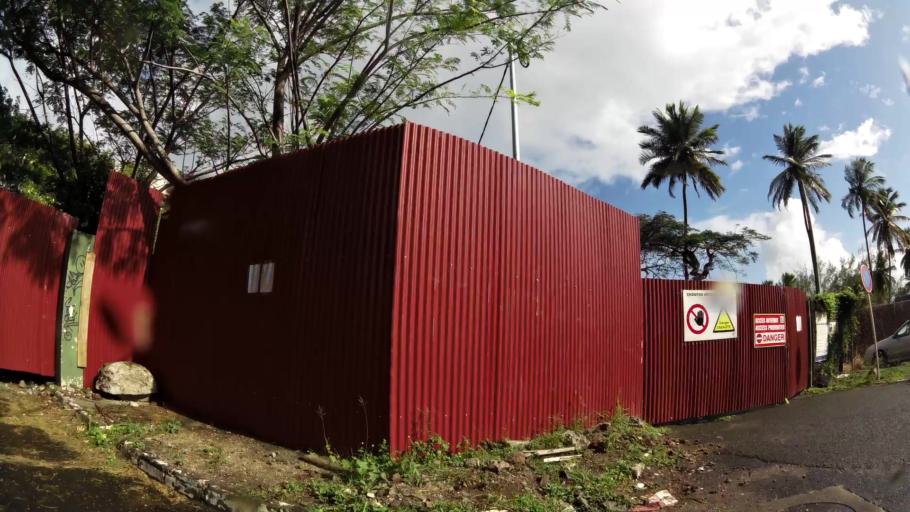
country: MQ
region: Martinique
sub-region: Martinique
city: Les Trois-Ilets
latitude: 14.5583
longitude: -61.0520
